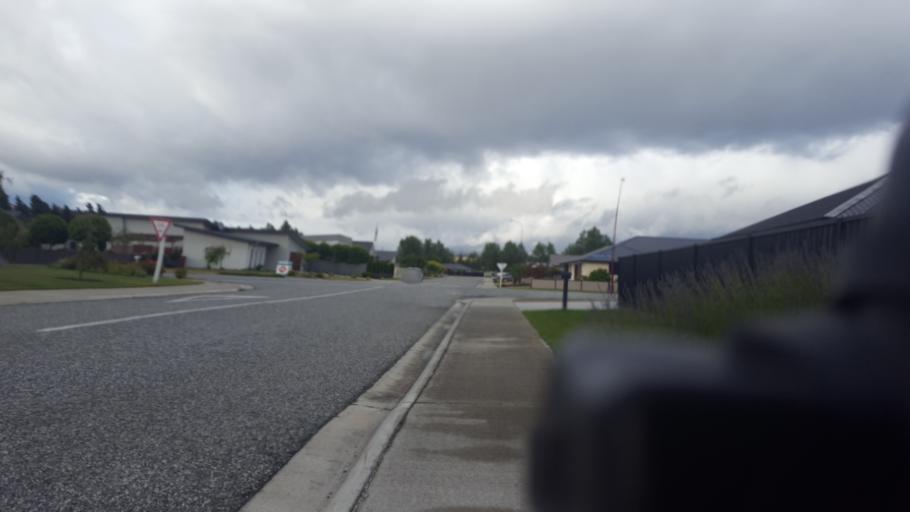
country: NZ
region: Otago
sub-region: Queenstown-Lakes District
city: Wanaka
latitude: -45.2393
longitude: 169.3790
